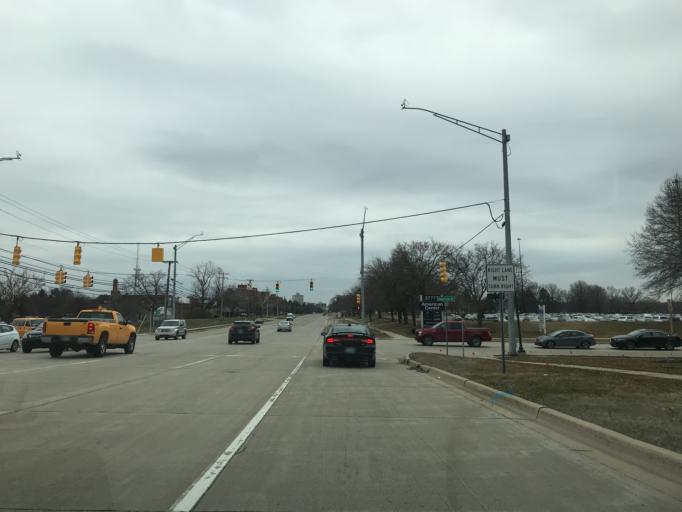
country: US
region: Michigan
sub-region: Oakland County
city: Franklin
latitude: 42.4925
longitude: -83.2986
